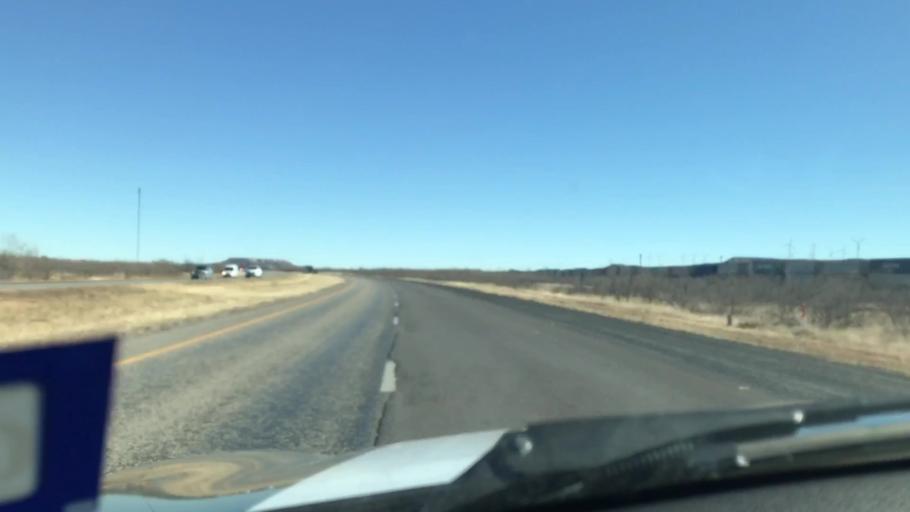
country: US
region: Texas
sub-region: Garza County
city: Post
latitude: 32.9886
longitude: -101.1384
